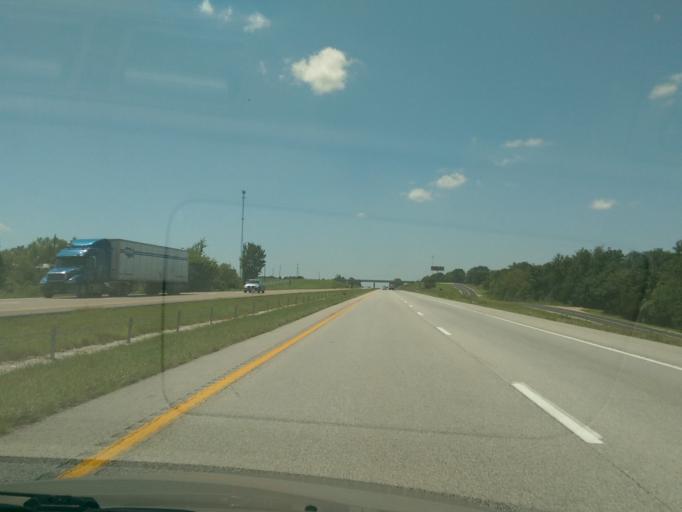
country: US
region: Missouri
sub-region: Cooper County
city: Boonville
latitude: 38.9353
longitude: -92.8082
